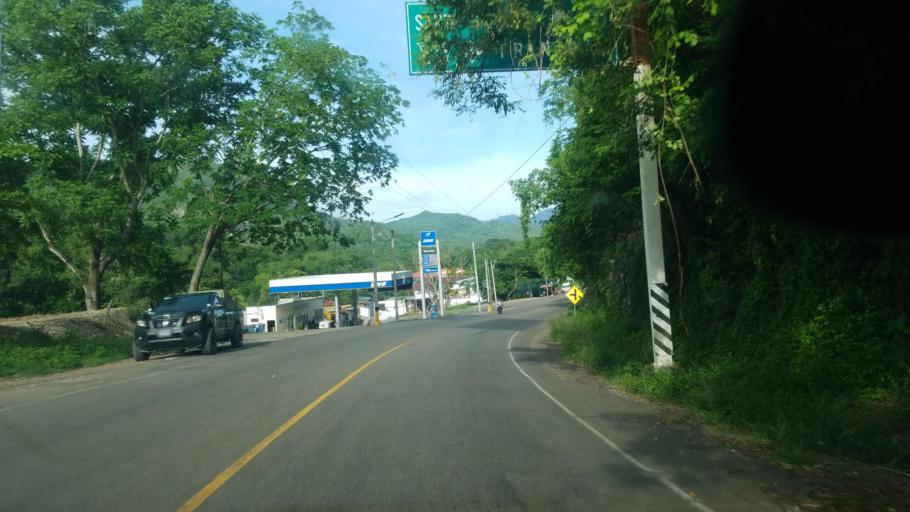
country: HN
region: Santa Barbara
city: Trinidad
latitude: 15.1394
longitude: -88.2350
